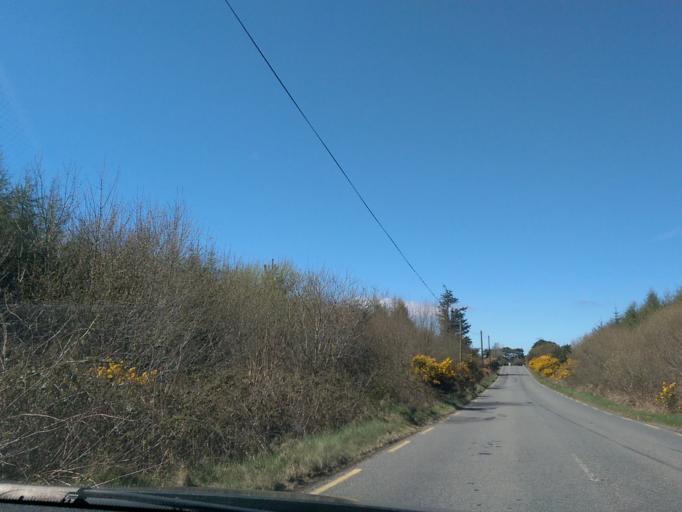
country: IE
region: Leinster
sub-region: Wicklow
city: Carnew
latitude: 52.8253
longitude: -6.5184
